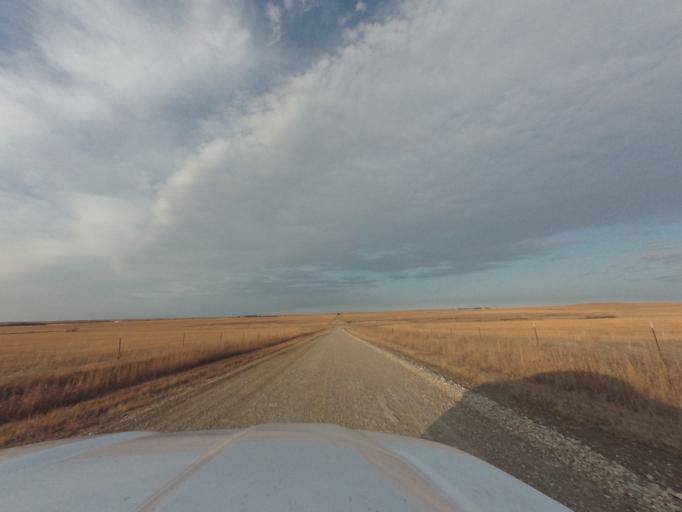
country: US
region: Kansas
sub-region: Chase County
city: Cottonwood Falls
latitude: 38.4930
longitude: -96.4079
